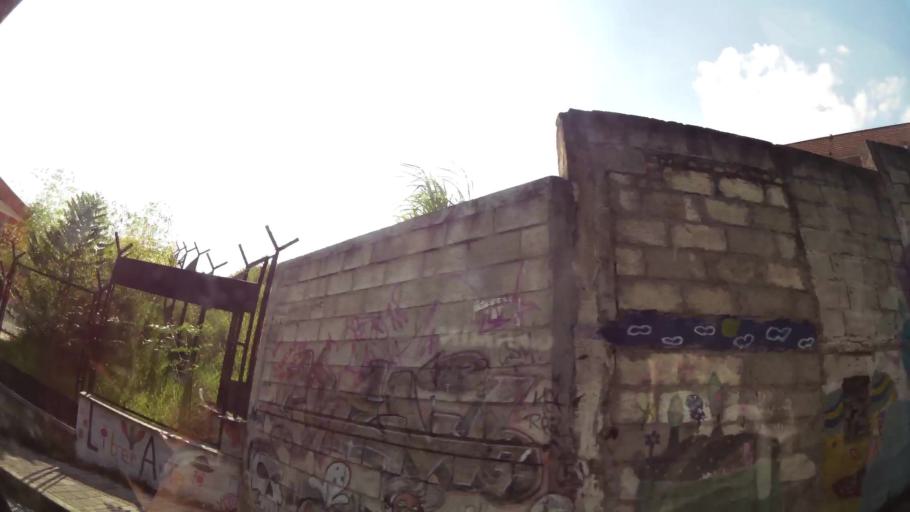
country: CO
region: Antioquia
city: Medellin
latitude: 6.2910
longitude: -75.5961
